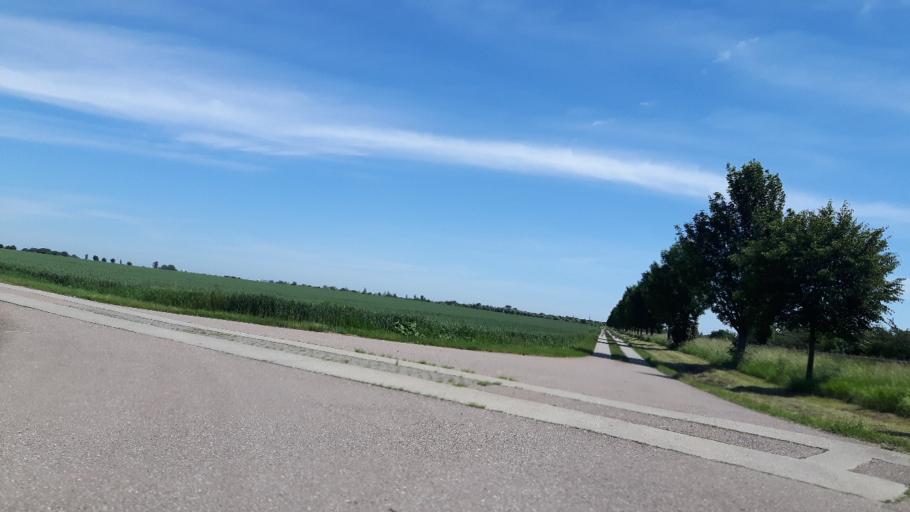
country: DE
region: Saxony-Anhalt
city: Granschutz
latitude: 51.2291
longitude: 12.0777
